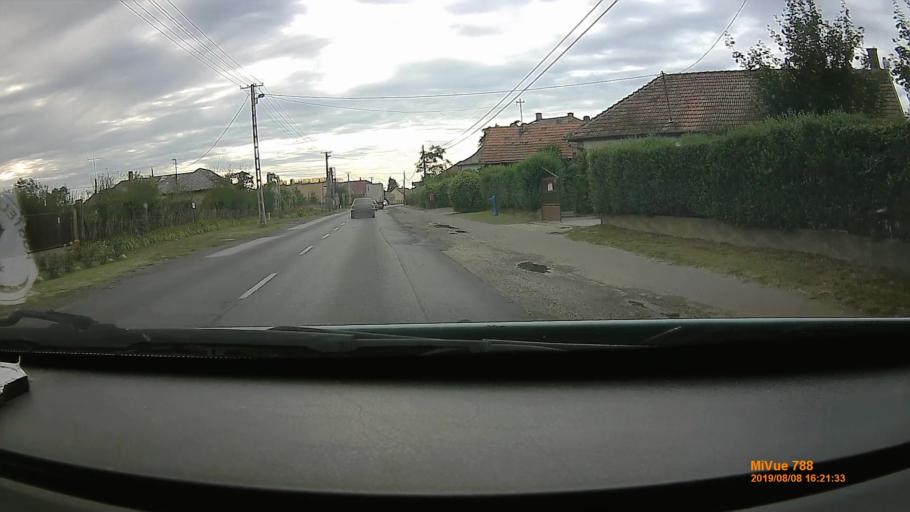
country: HU
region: Szabolcs-Szatmar-Bereg
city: Nyirmeggyes
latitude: 47.9692
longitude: 22.2578
